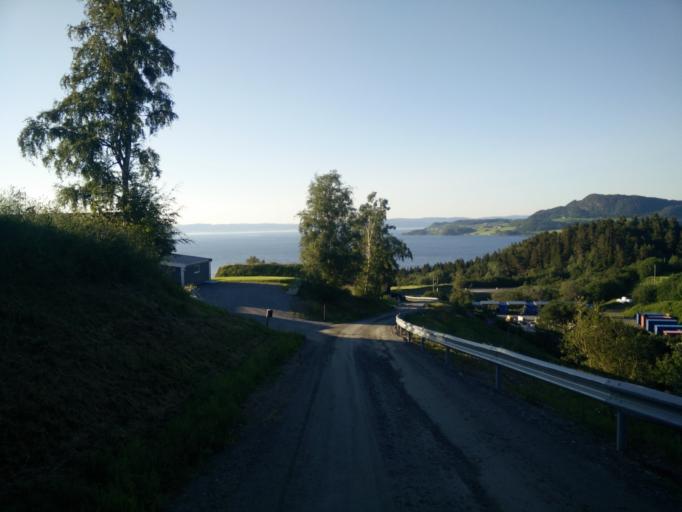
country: NO
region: Sor-Trondelag
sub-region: Skaun
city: Borsa
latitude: 63.3433
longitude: 10.0398
